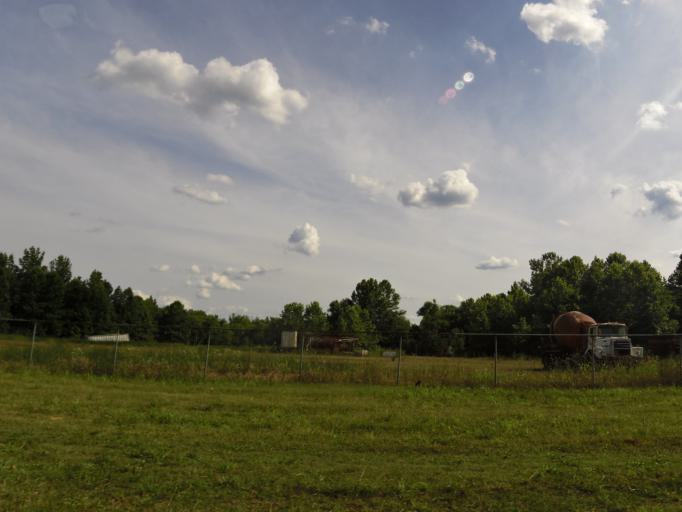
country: US
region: Tennessee
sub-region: Carroll County
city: Bruceton
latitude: 36.0376
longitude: -88.2333
